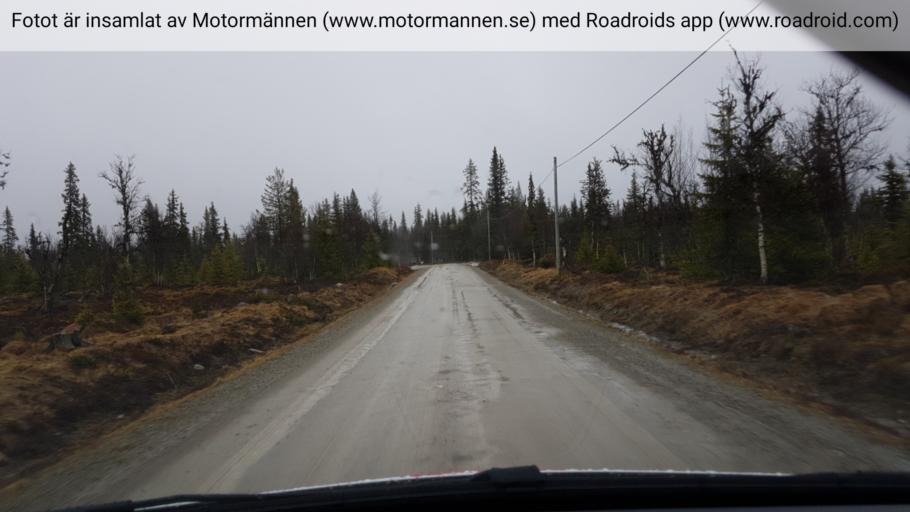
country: SE
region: Jaemtland
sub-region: Are Kommun
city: Jarpen
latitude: 62.5975
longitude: 13.2930
